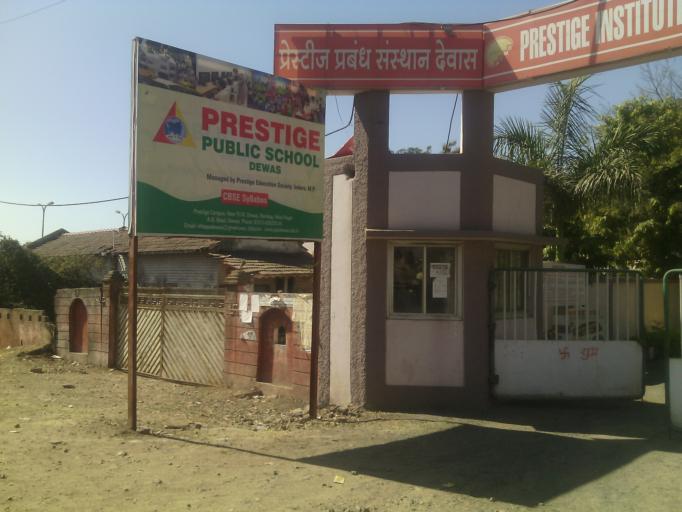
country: IN
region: Madhya Pradesh
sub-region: Dewas
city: Dewas
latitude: 22.9471
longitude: 76.0317
